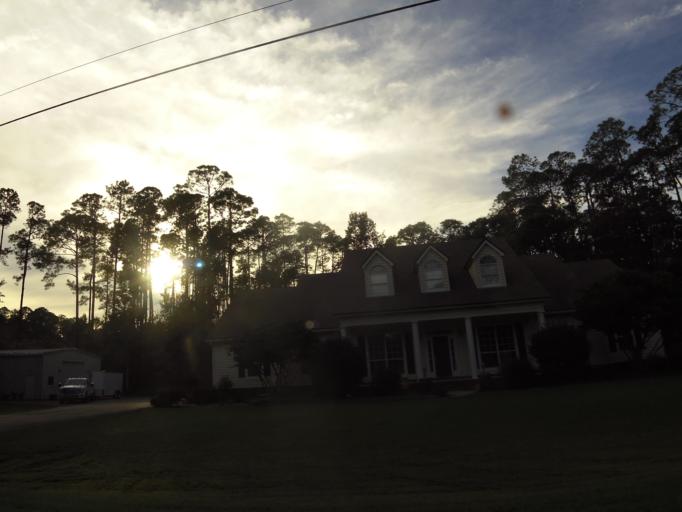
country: US
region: Florida
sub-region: Saint Johns County
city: Fruit Cove
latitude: 30.1570
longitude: -81.5715
